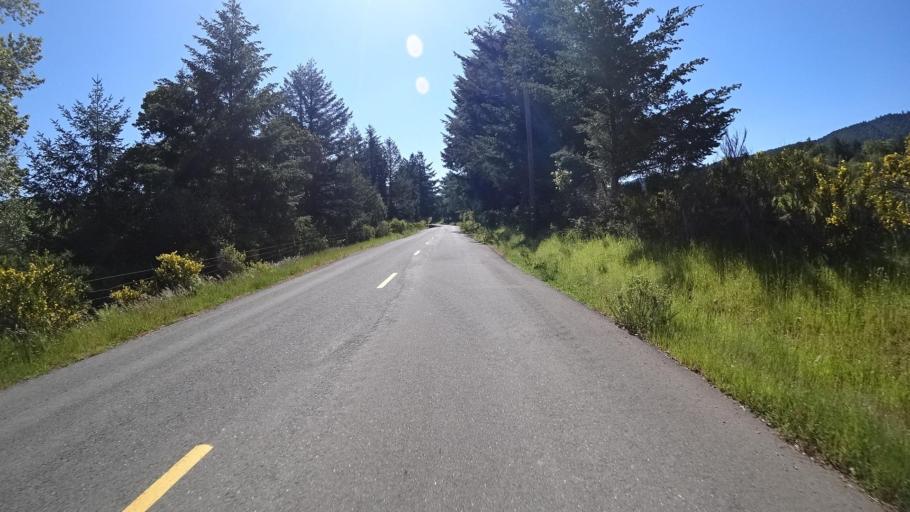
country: US
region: California
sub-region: Humboldt County
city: Rio Dell
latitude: 40.2479
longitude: -124.1683
